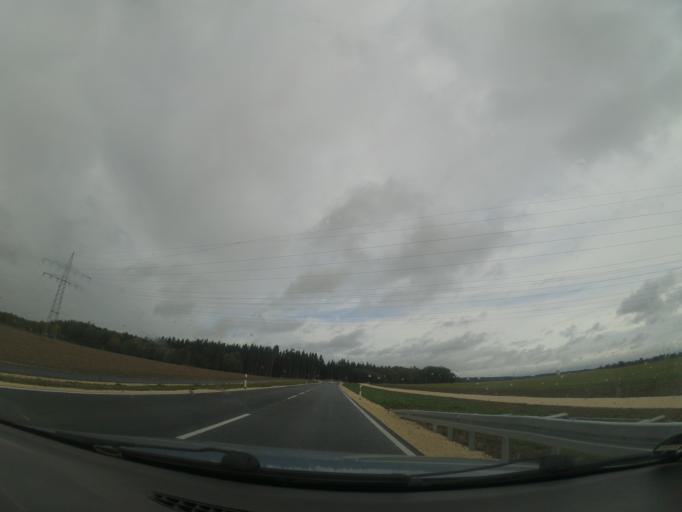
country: DE
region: Baden-Wuerttemberg
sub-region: Tuebingen Region
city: Beimerstetten
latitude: 48.4724
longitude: 9.9676
